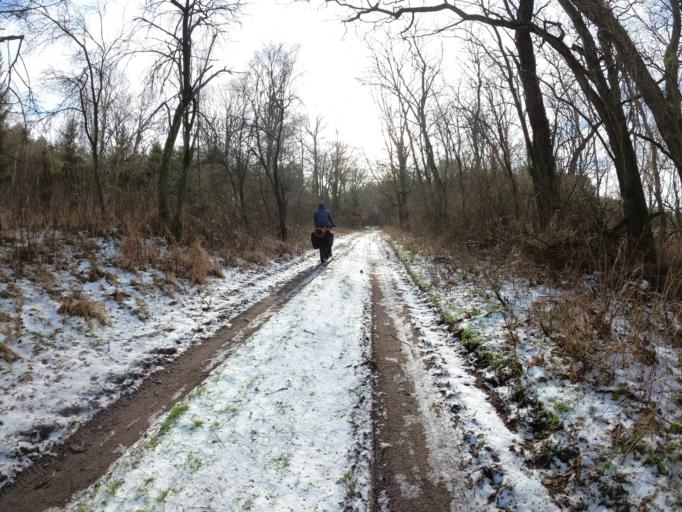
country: PL
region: Lubusz
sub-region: Powiat slubicki
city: Cybinka
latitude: 52.2680
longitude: 14.7900
